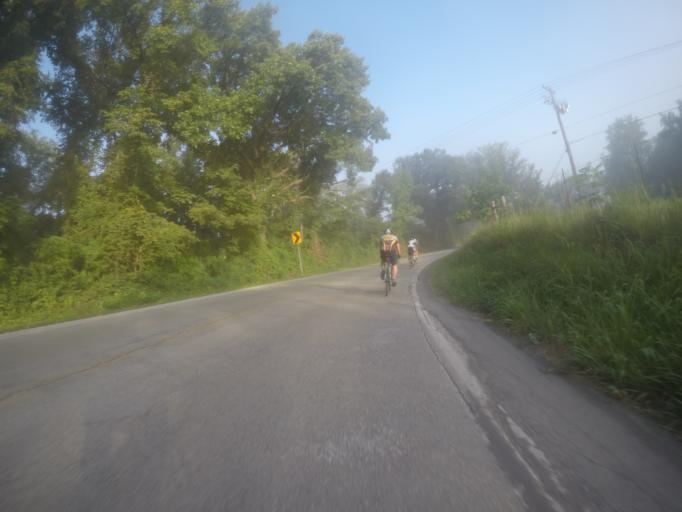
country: US
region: Kansas
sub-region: Leavenworth County
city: Lansing
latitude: 39.2639
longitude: -94.8883
